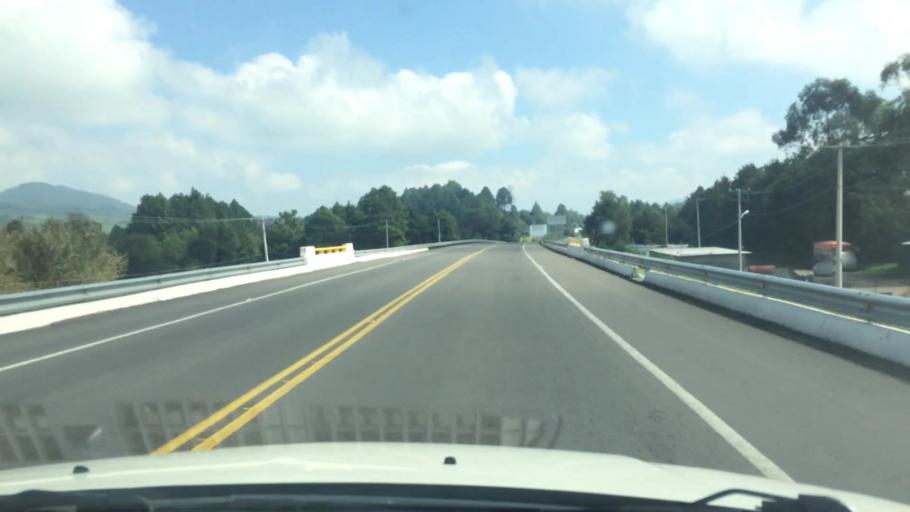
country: MX
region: Mexico
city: Amanalco de Becerra
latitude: 19.3423
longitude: -99.9929
